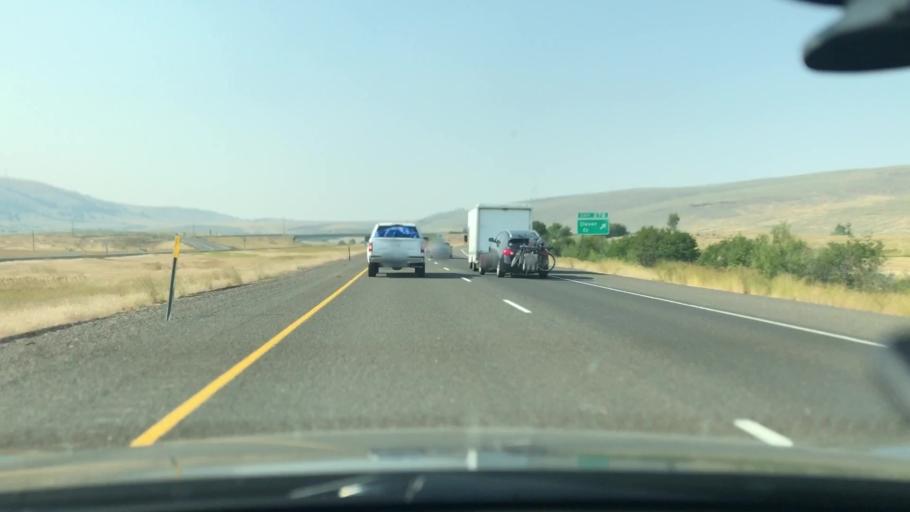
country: US
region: Oregon
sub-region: Union County
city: Union
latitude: 45.1195
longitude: -117.9609
